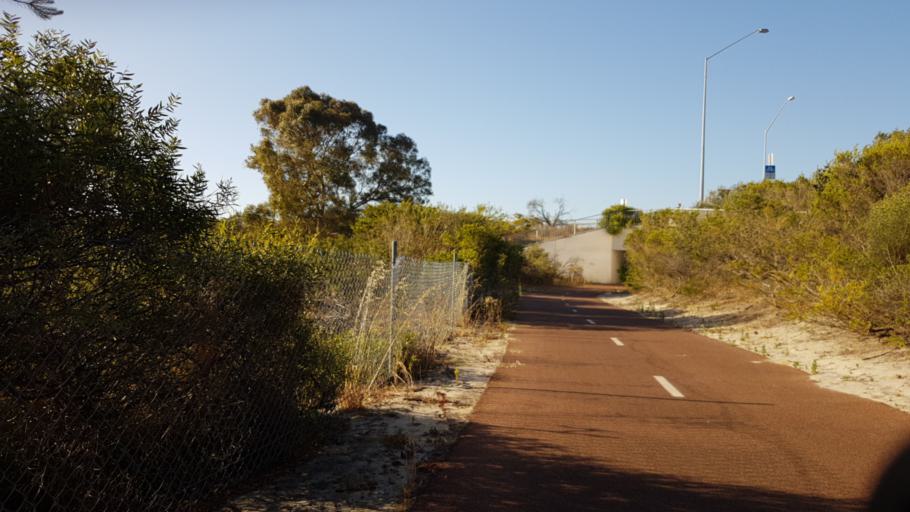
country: AU
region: Western Australia
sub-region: Kwinana
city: Bertram
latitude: -32.2558
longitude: 115.8520
